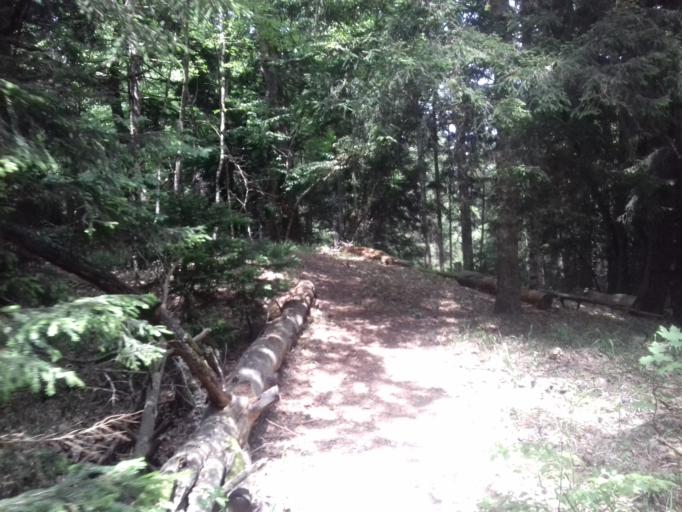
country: GE
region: Samtskhe-Javakheti
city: Borjomi
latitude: 41.8254
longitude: 43.3302
